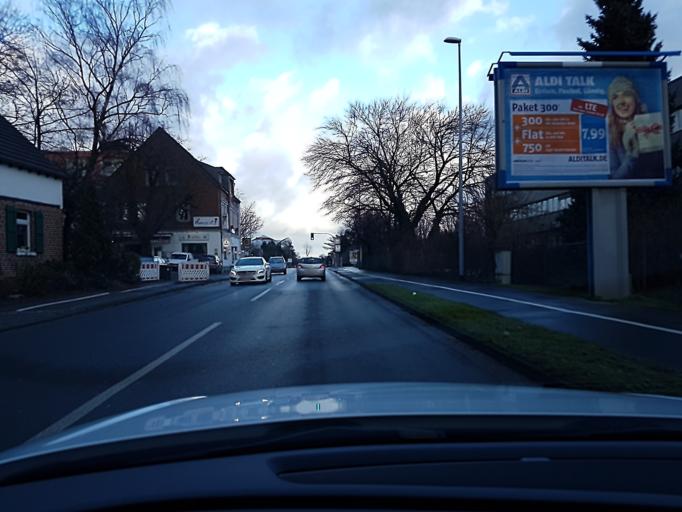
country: DE
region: North Rhine-Westphalia
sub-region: Regierungsbezirk Dusseldorf
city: Muelheim (Ruhr)
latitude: 51.3934
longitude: 6.8717
